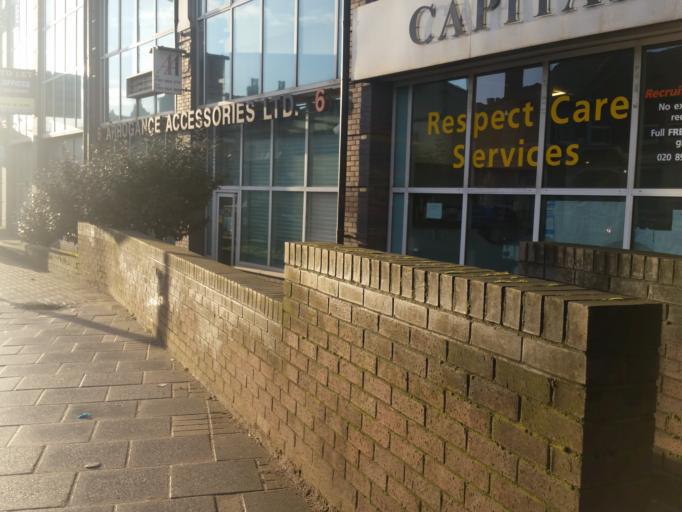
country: GB
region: England
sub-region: Greater London
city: Hammersmith
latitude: 51.5295
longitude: -0.2371
